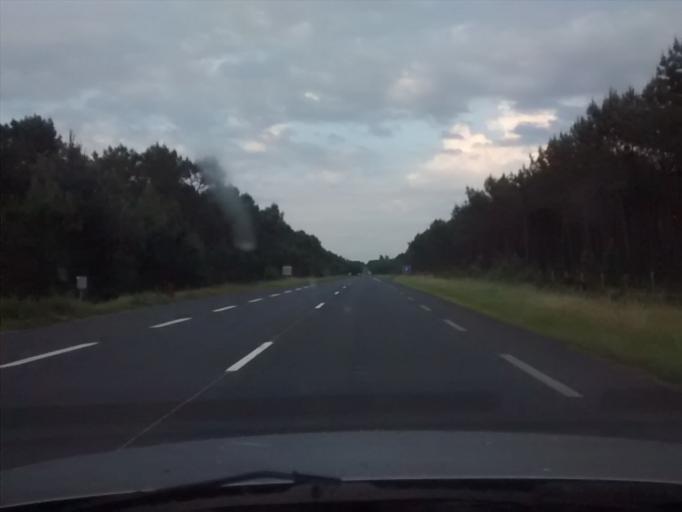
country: FR
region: Pays de la Loire
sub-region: Departement de la Sarthe
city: Saint-Mars-la-Briere
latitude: 48.0034
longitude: 0.3905
